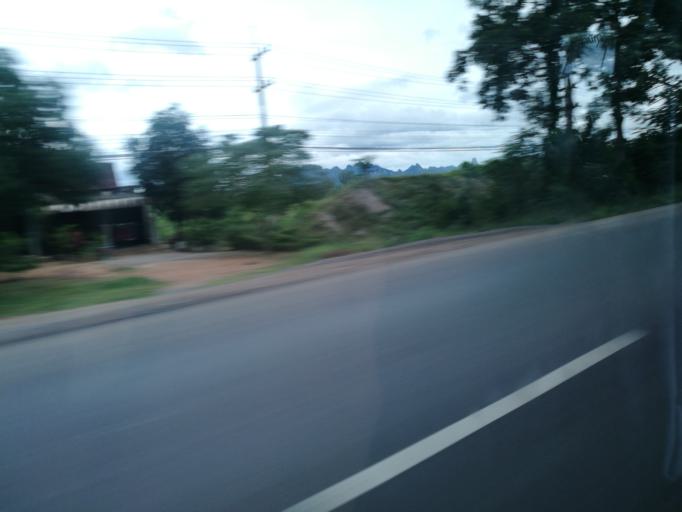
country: TH
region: Prachuap Khiri Khan
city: Sam Roi Yot
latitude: 12.3167
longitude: 99.8781
